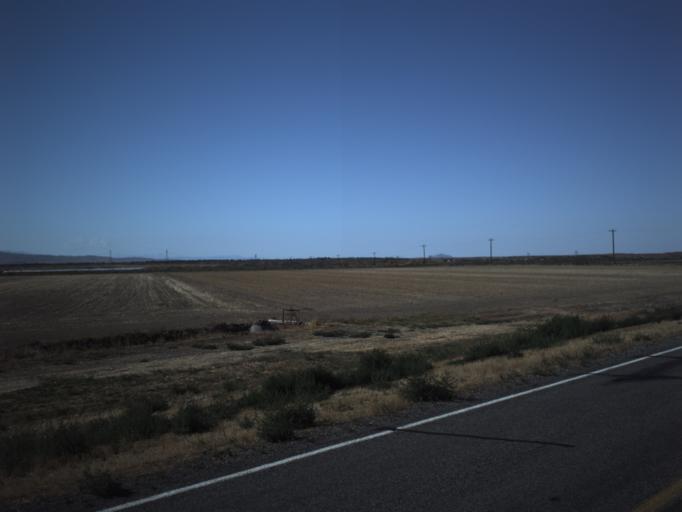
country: US
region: Utah
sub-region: Millard County
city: Delta
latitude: 39.5127
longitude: -112.3758
